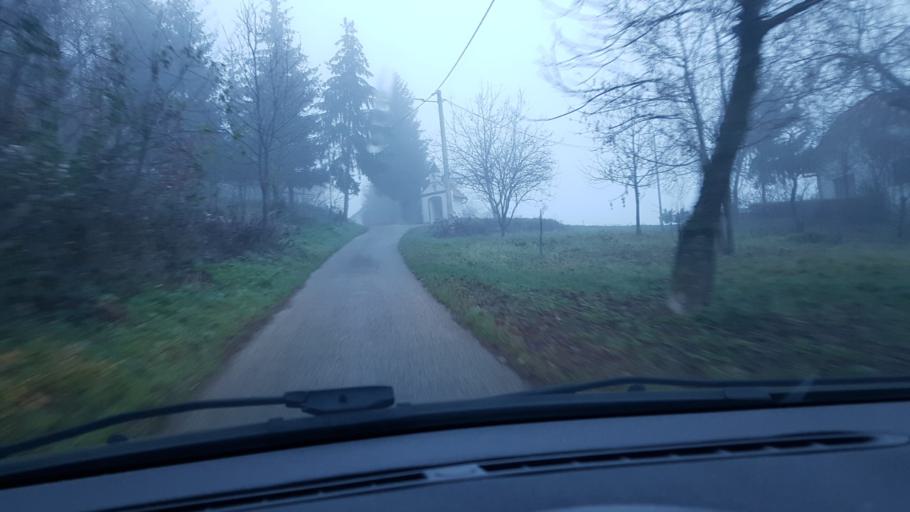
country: HR
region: Krapinsko-Zagorska
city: Pregrada
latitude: 46.2005
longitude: 15.7810
